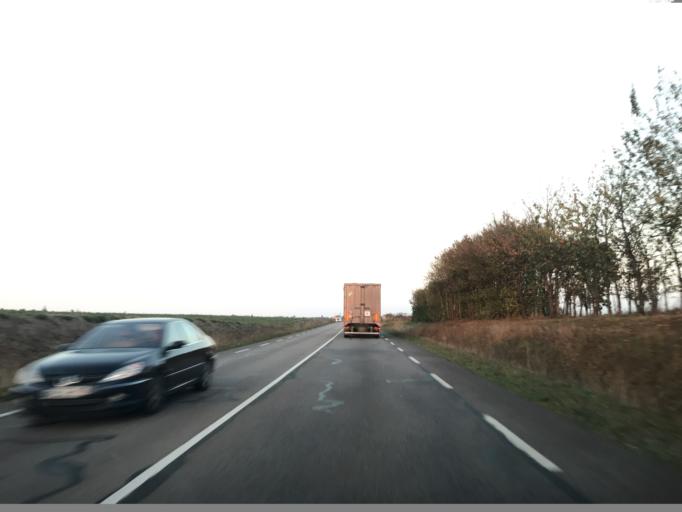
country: FR
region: Haute-Normandie
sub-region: Departement de l'Eure
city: Verneuil-sur-Avre
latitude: 48.7257
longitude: 0.8974
